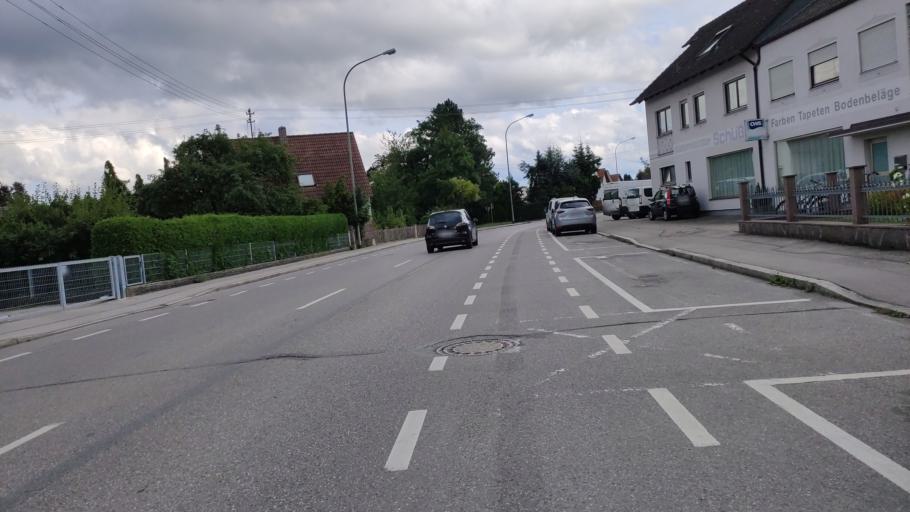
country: DE
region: Bavaria
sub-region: Swabia
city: Konigsbrunn
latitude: 48.2637
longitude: 10.8873
